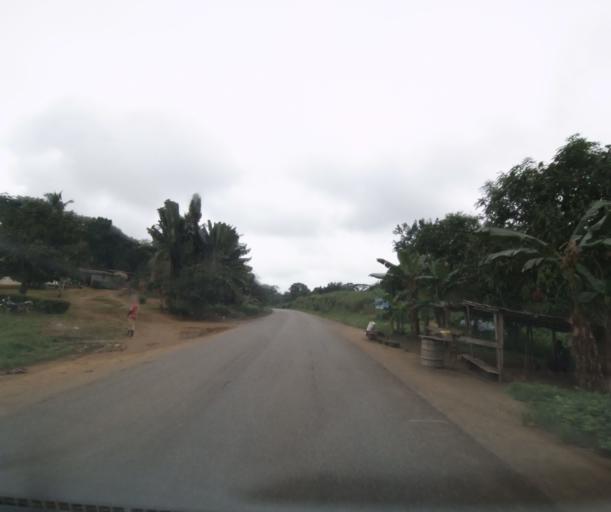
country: CM
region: Littoral
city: Edea
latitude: 3.6967
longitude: 10.1042
